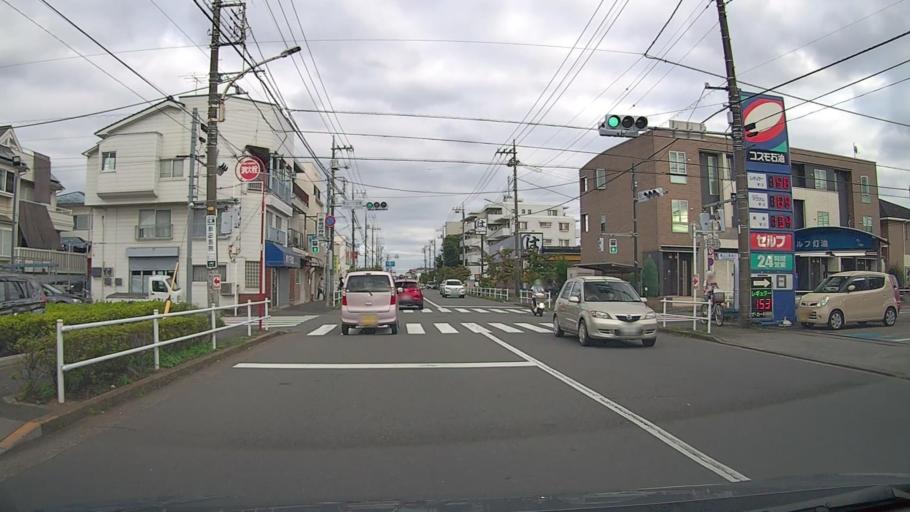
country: JP
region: Tokyo
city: Tanashicho
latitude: 35.7479
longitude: 139.5125
